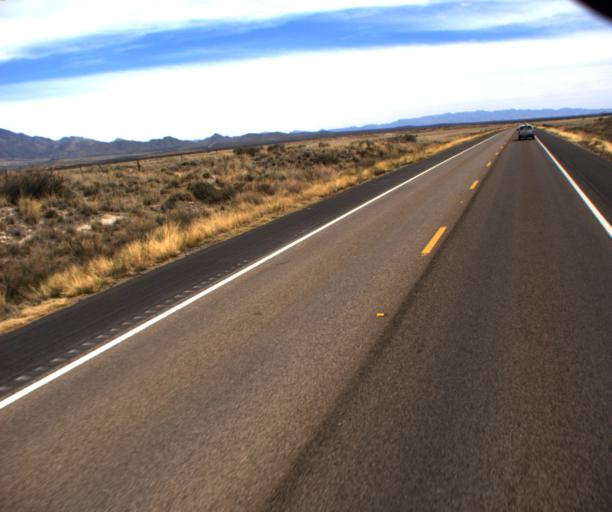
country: US
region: Arizona
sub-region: Cochise County
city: Willcox
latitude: 32.2133
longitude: -109.7811
